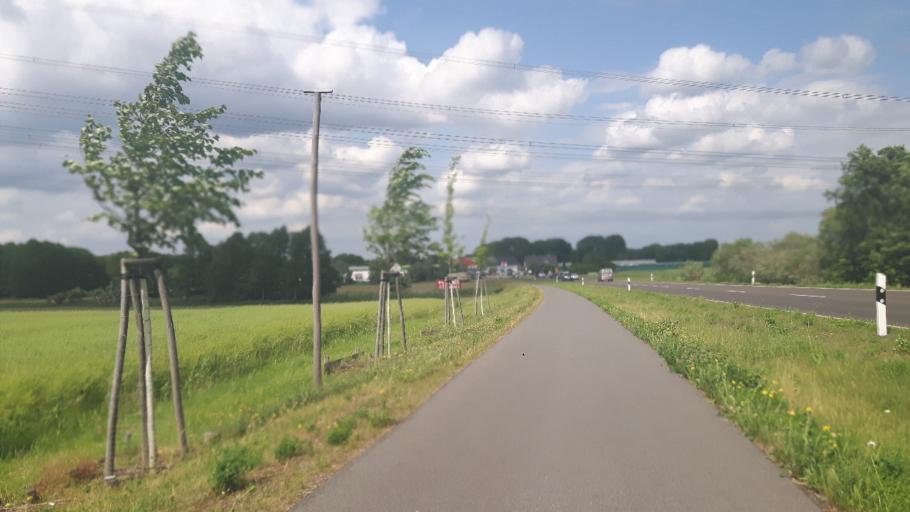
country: DE
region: Berlin
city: Buch
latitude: 52.6181
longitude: 13.5405
